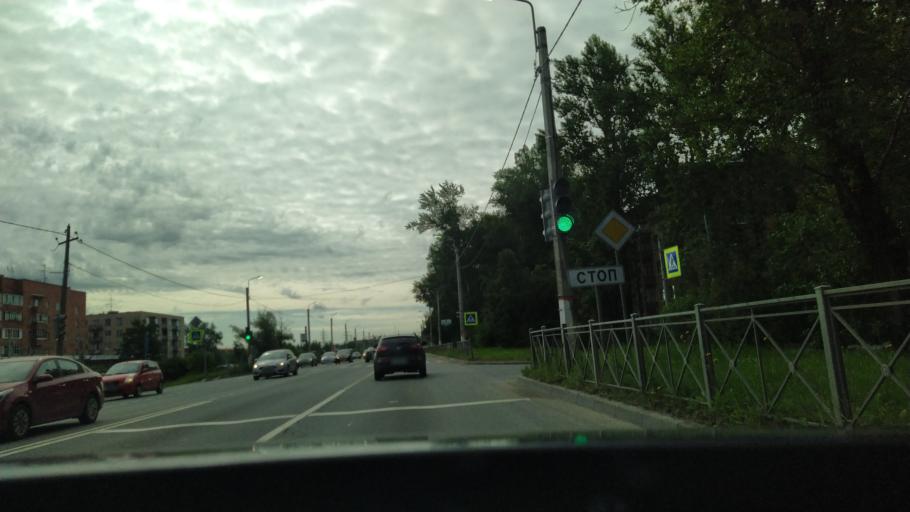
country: RU
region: Leningrad
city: Tosno
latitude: 59.5581
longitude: 30.8457
